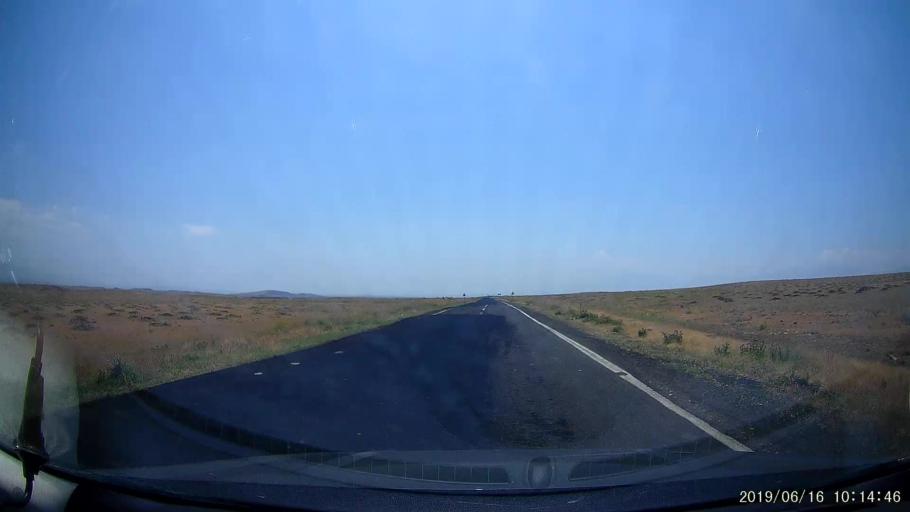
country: TR
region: Igdir
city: Tuzluca
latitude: 40.1819
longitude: 43.6697
